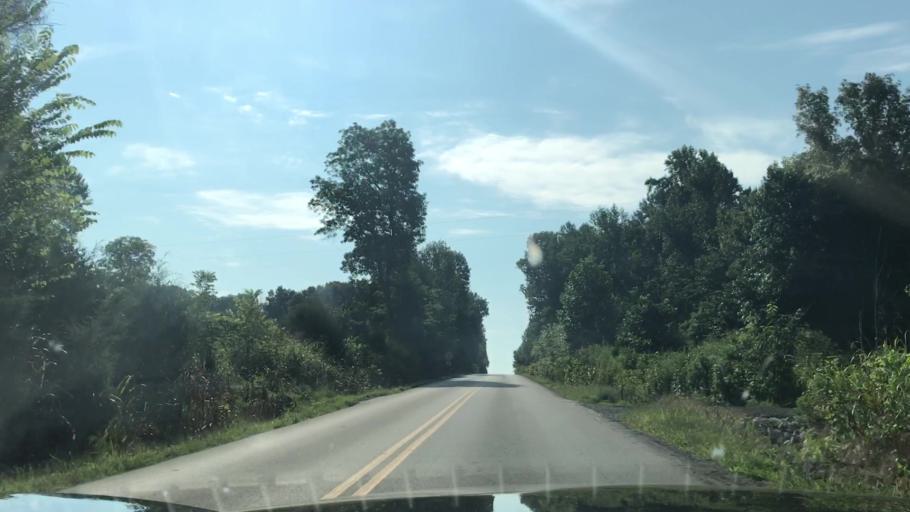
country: US
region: Kentucky
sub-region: Green County
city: Greensburg
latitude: 37.2266
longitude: -85.6701
